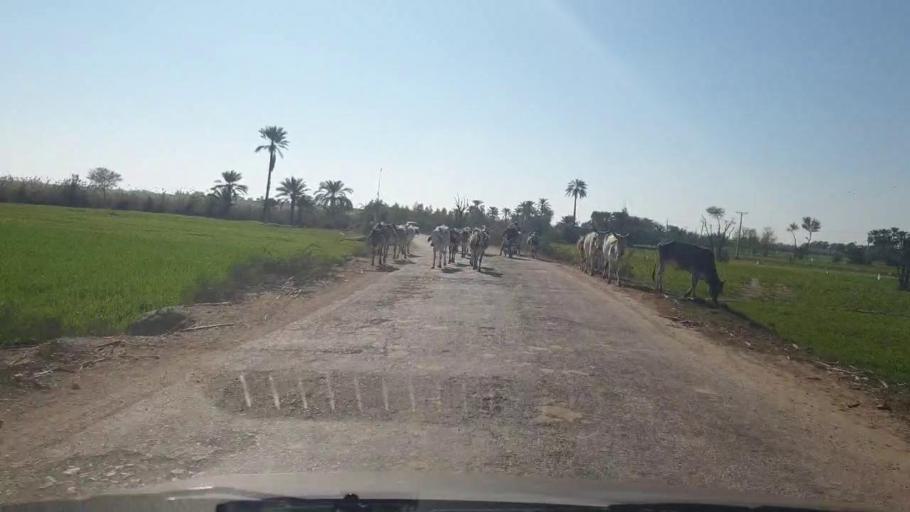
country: PK
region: Sindh
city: Bozdar
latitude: 27.2415
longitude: 68.6518
